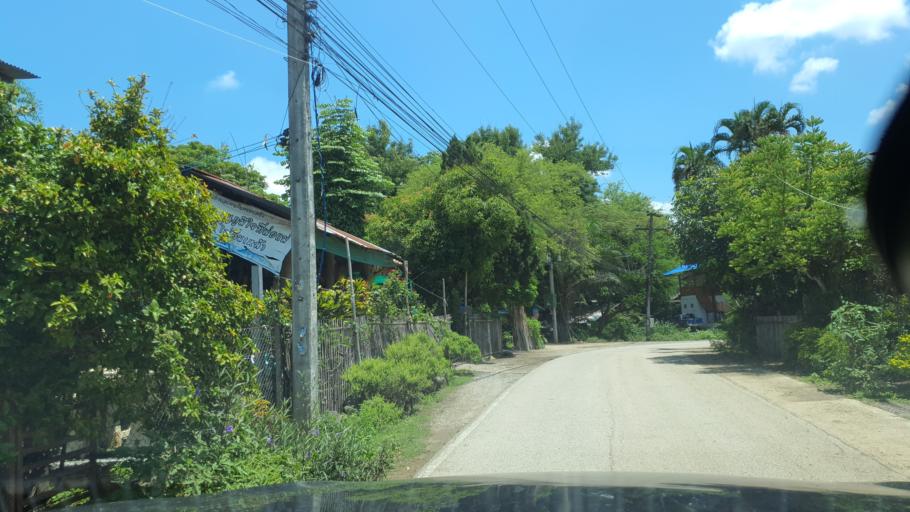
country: TH
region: Chiang Mai
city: Mae On
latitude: 18.8152
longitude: 99.2597
